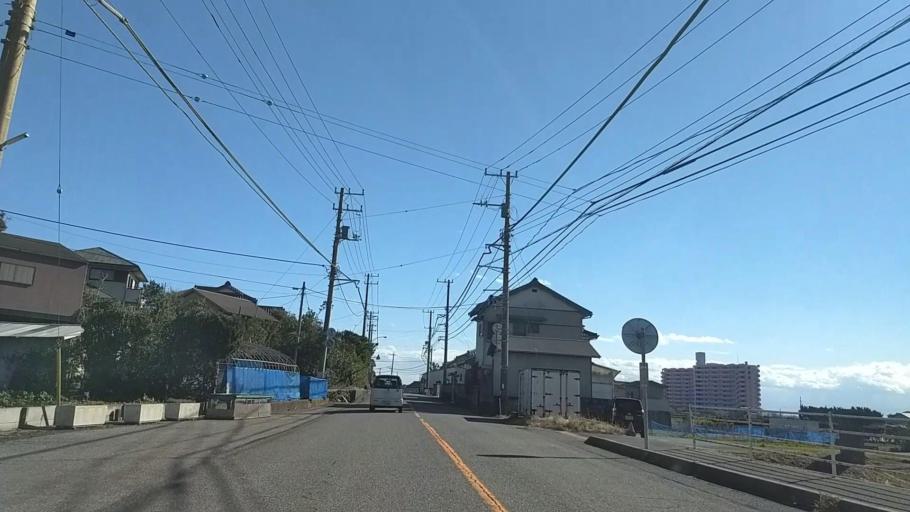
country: JP
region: Chiba
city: Tateyama
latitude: 34.9079
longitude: 139.8790
